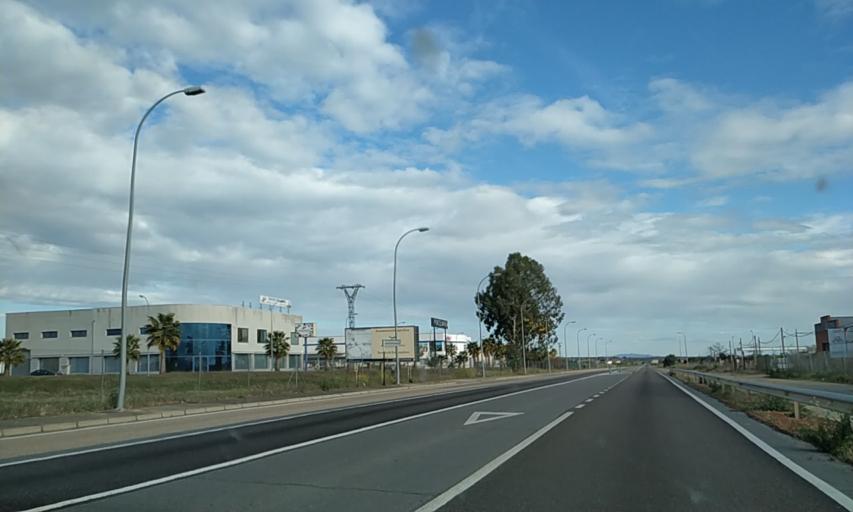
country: ES
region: Extremadura
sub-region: Provincia de Caceres
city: Moraleja
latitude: 40.0580
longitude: -6.6464
